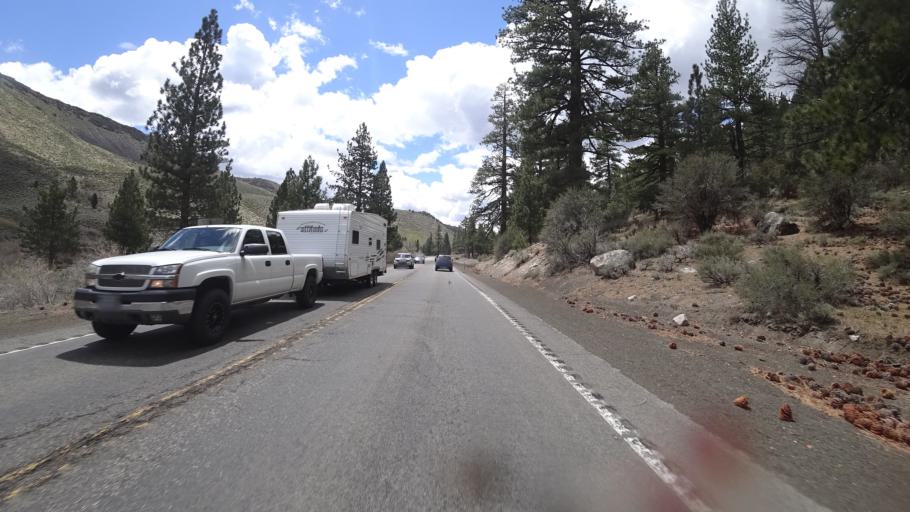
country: US
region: California
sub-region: Mono County
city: Bridgeport
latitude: 38.3966
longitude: -119.4531
